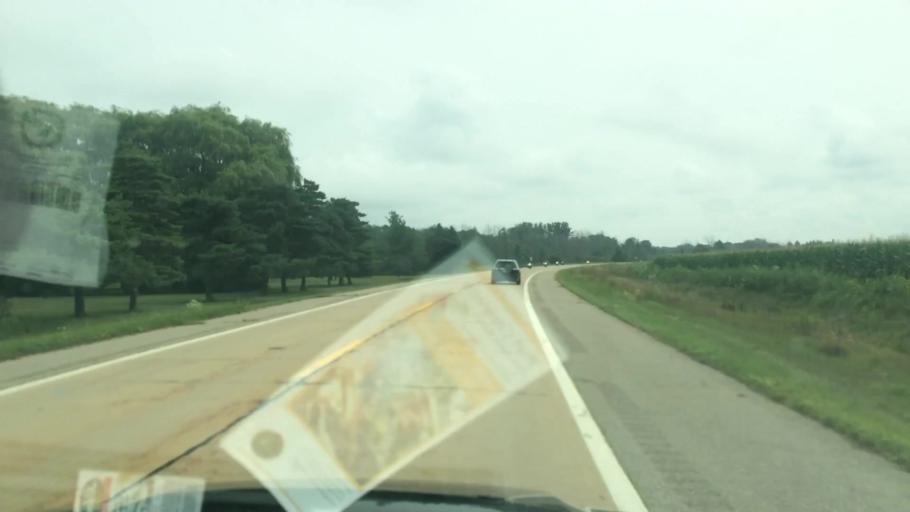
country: US
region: Michigan
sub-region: Huron County
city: Bad Axe
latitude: 44.0438
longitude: -82.8805
